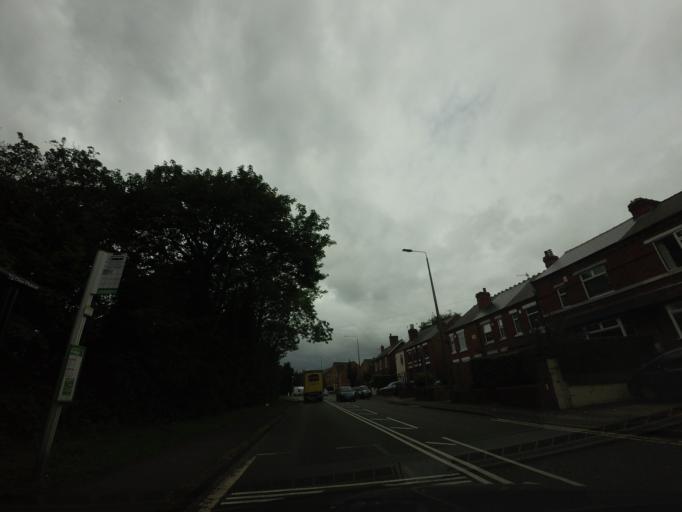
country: GB
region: England
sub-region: Nottinghamshire
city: Kimberley
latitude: 52.9993
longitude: -1.2411
